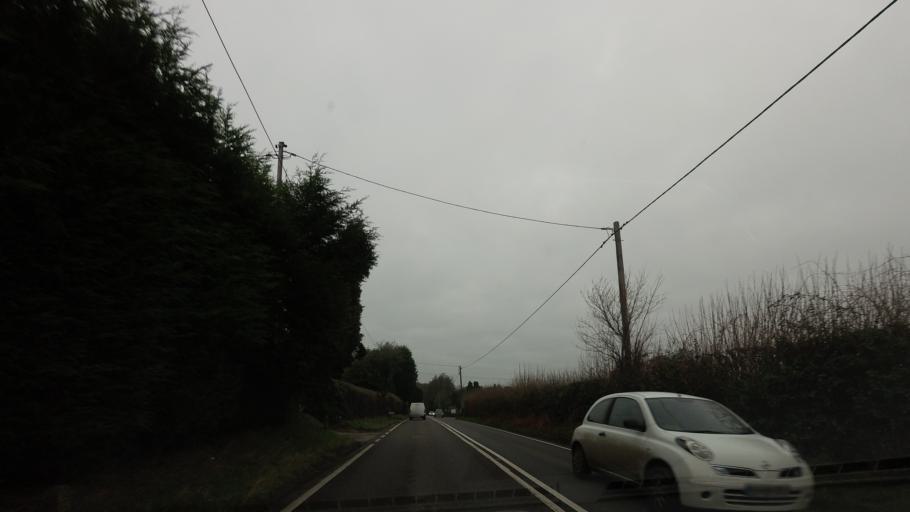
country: GB
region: England
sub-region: East Sussex
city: Saint Leonards-on-Sea
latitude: 50.9108
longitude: 0.5449
